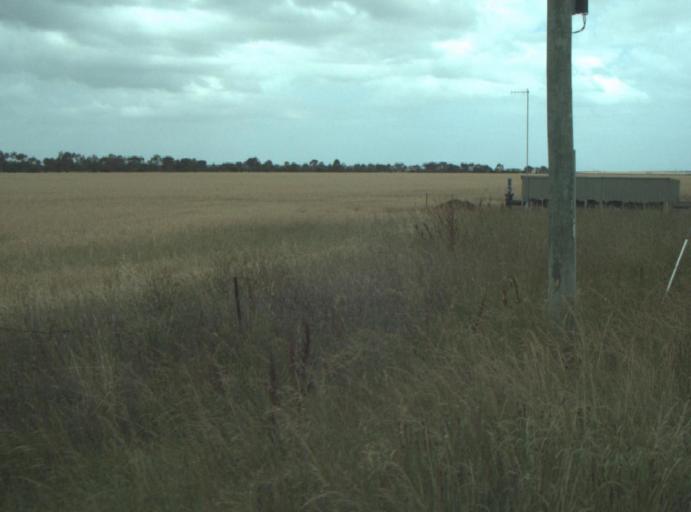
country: AU
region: Victoria
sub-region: Greater Geelong
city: Leopold
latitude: -38.1842
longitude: 144.4192
